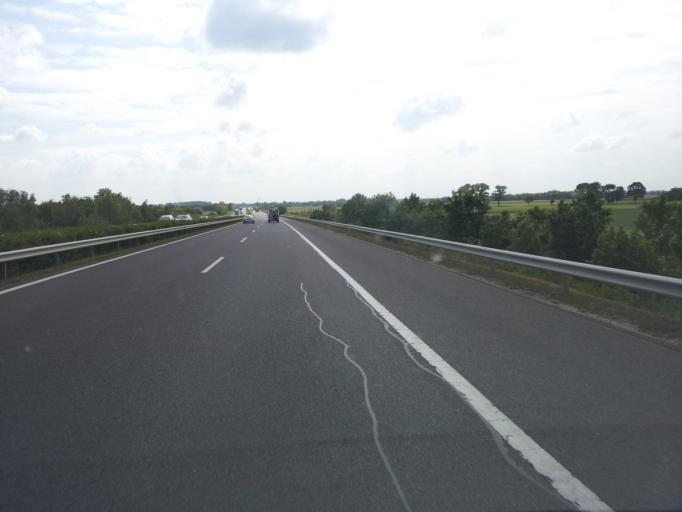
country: HU
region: Borsod-Abauj-Zemplen
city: Hejobaba
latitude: 47.8753
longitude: 20.9261
